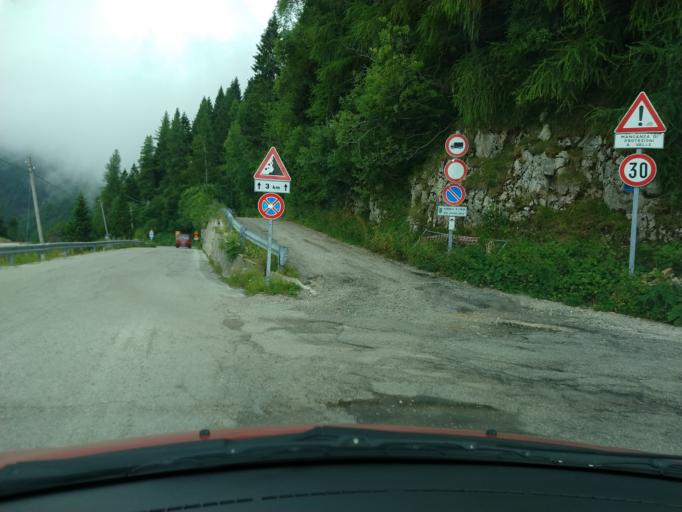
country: IT
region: Veneto
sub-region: Provincia di Vicenza
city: Longhi
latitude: 45.8787
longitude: 11.3029
